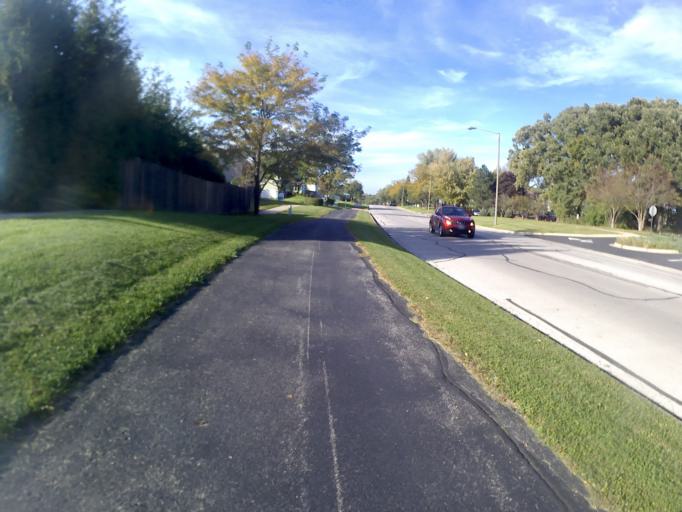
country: US
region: Illinois
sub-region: DuPage County
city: Woodridge
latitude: 41.7387
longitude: -88.0474
